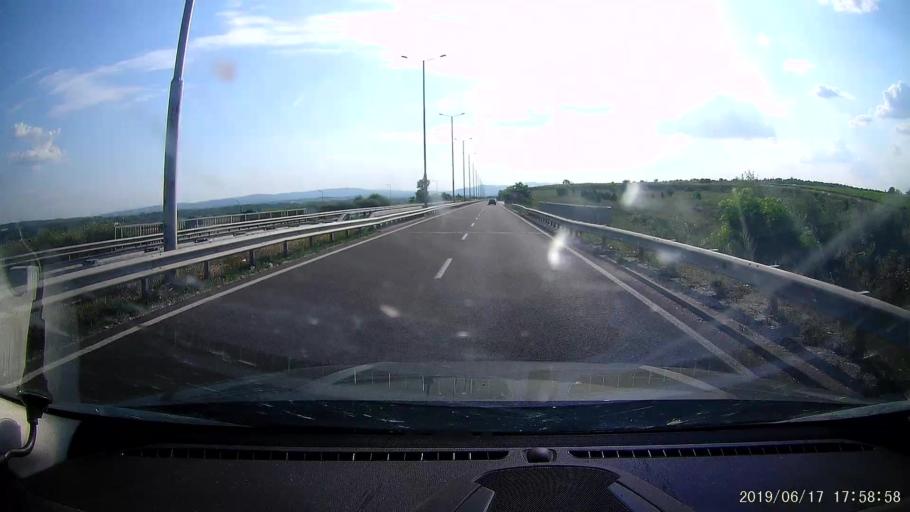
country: BG
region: Khaskovo
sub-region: Obshtina Svilengrad
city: Svilengrad
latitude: 41.7256
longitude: 26.3100
